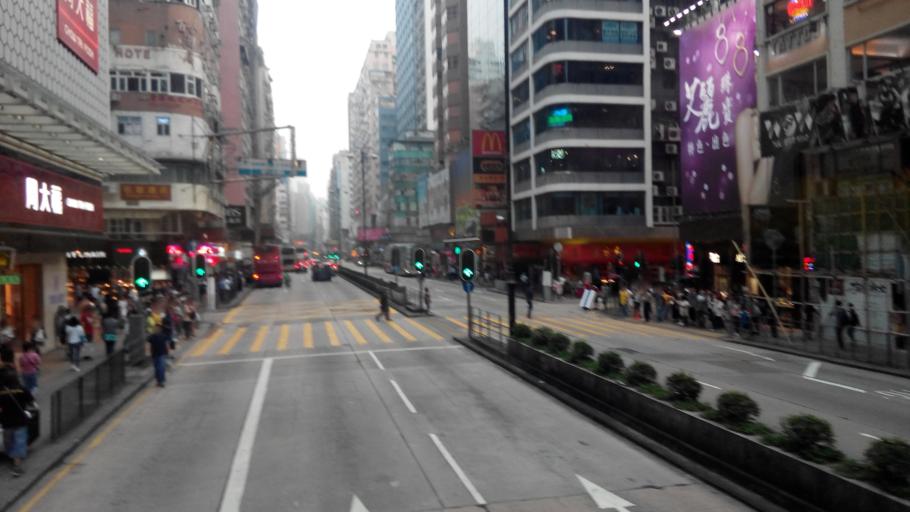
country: HK
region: Kowloon City
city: Kowloon
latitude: 22.3158
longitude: 114.1699
